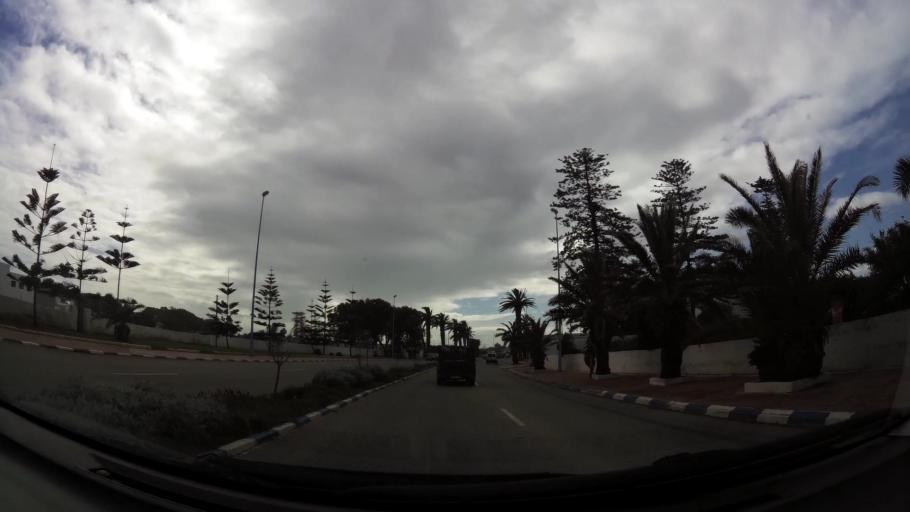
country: MA
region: Doukkala-Abda
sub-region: El-Jadida
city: El Jadida
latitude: 33.2437
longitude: -8.4723
